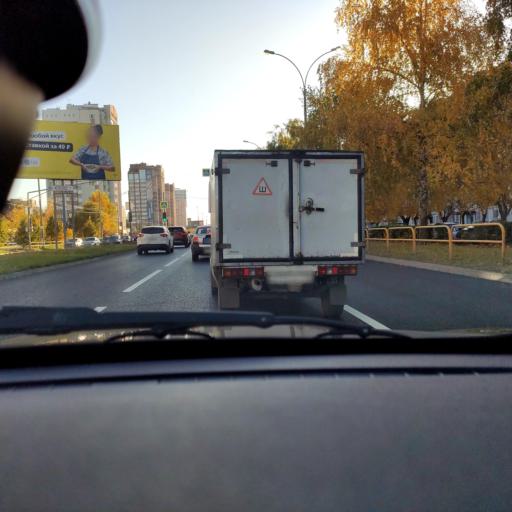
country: RU
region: Samara
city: Tol'yatti
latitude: 53.5140
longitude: 49.2888
